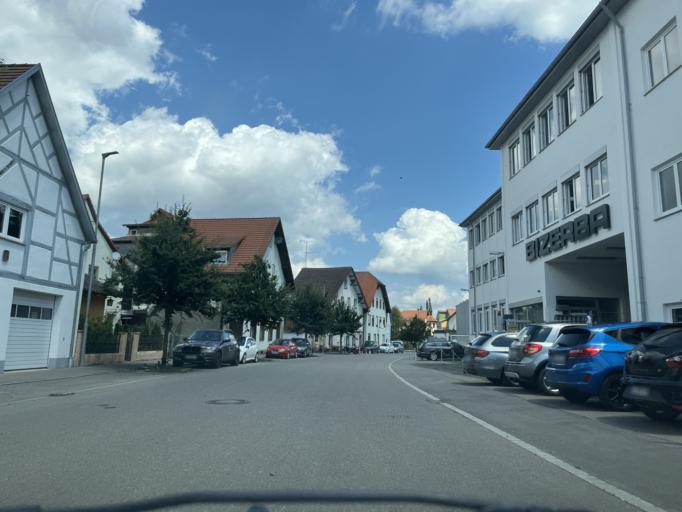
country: DE
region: Baden-Wuerttemberg
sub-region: Tuebingen Region
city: Messkirch
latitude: 47.9921
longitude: 9.1120
